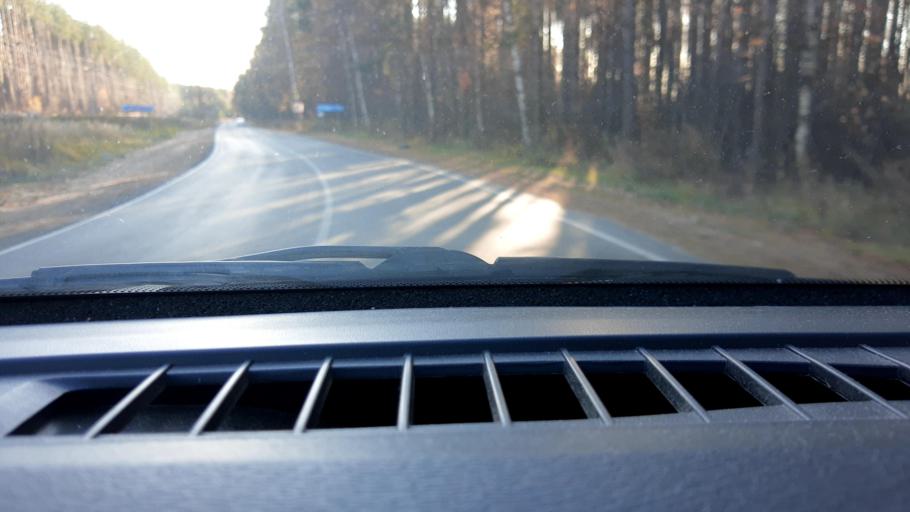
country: RU
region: Nizjnij Novgorod
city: Neklyudovo
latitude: 56.4451
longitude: 43.8993
